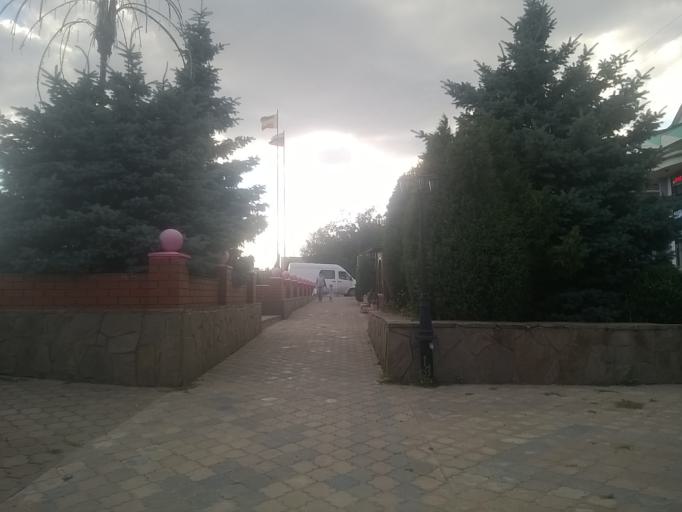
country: RU
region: Rostov
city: Donetsk
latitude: 48.3306
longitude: 39.9543
